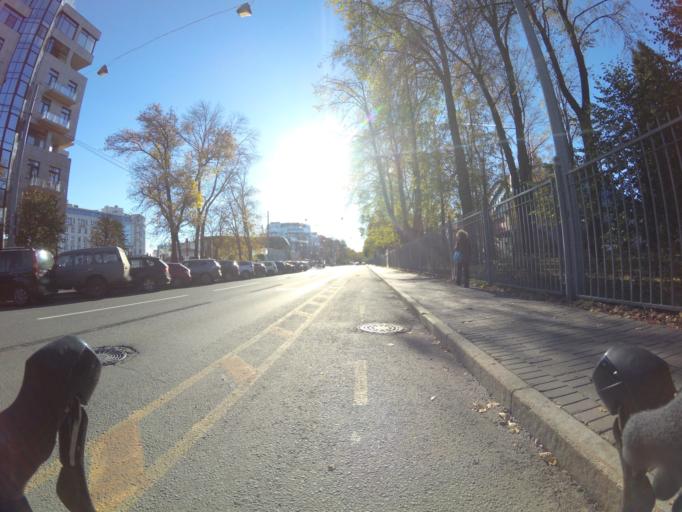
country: RU
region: Leningrad
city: Krestovskiy ostrov
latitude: 59.9728
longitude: 30.2585
